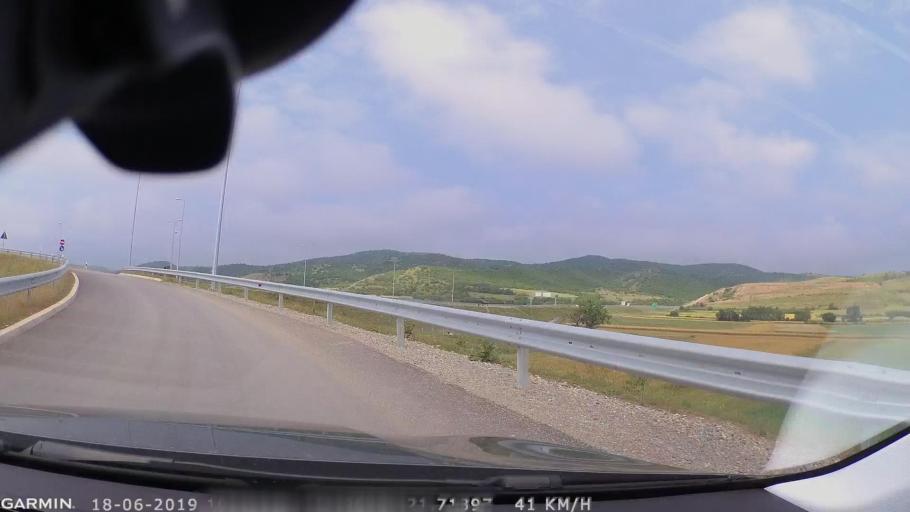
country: MK
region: Petrovec
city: Sredno Konjare
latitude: 41.9444
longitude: 21.8057
